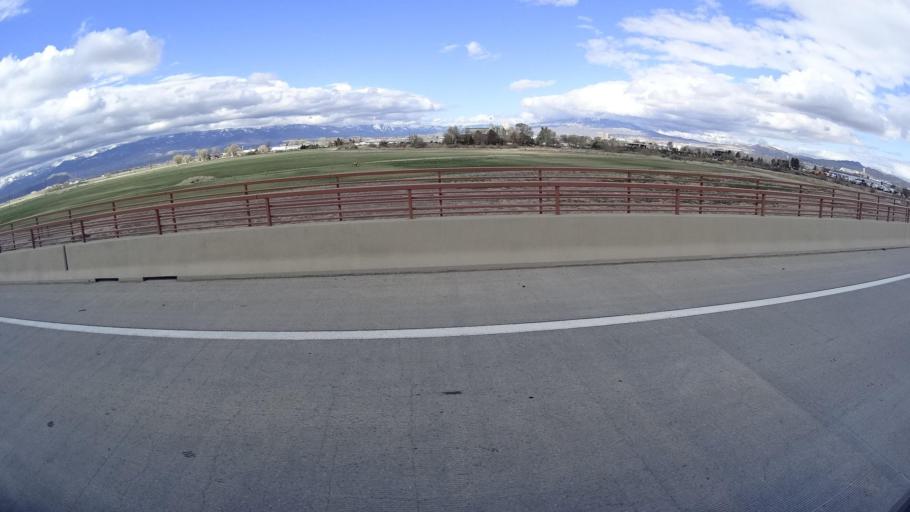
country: US
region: Nevada
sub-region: Washoe County
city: Sparks
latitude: 39.5178
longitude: -119.7099
